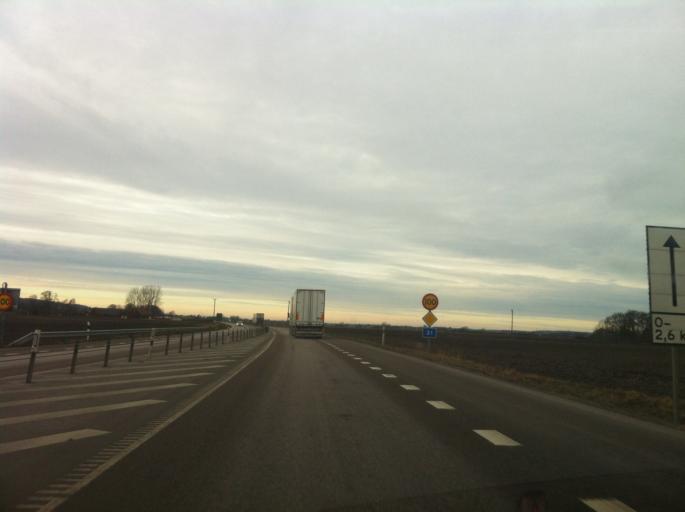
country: SE
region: Skane
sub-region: Astorps Kommun
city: Kvidinge
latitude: 56.1329
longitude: 13.0323
